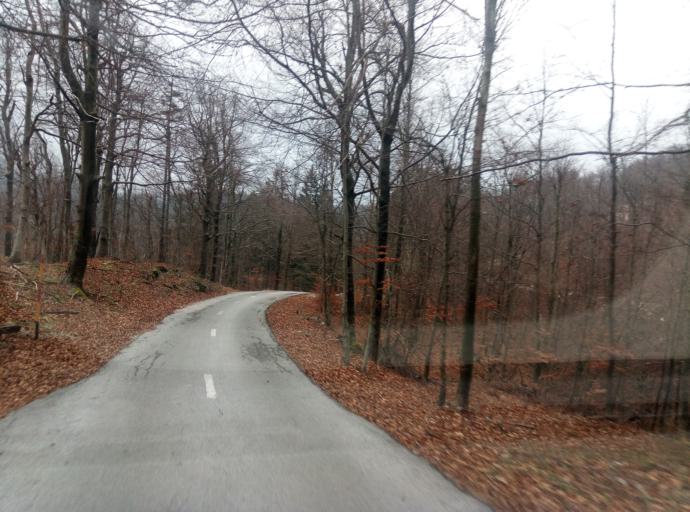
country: SI
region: Vipava
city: Vipava
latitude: 45.9060
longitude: 14.0263
